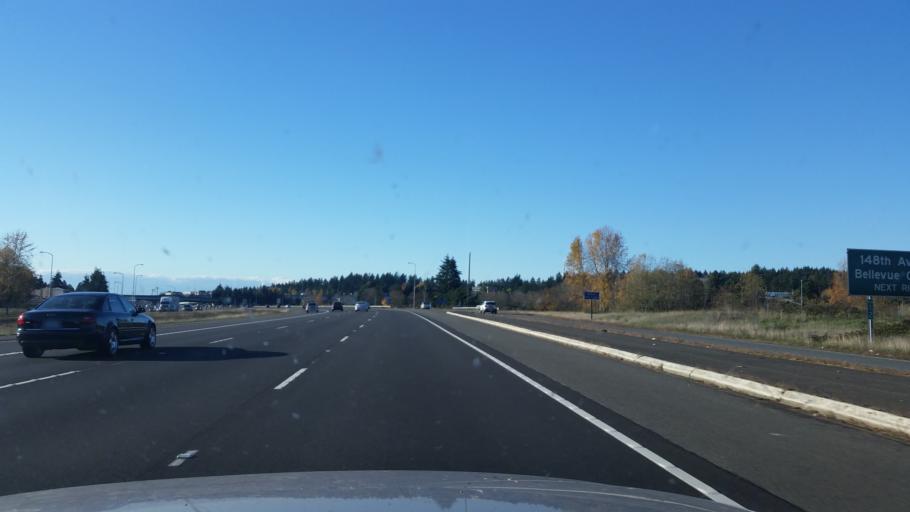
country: US
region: Washington
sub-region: King County
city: Eastgate
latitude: 47.5776
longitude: -122.1299
